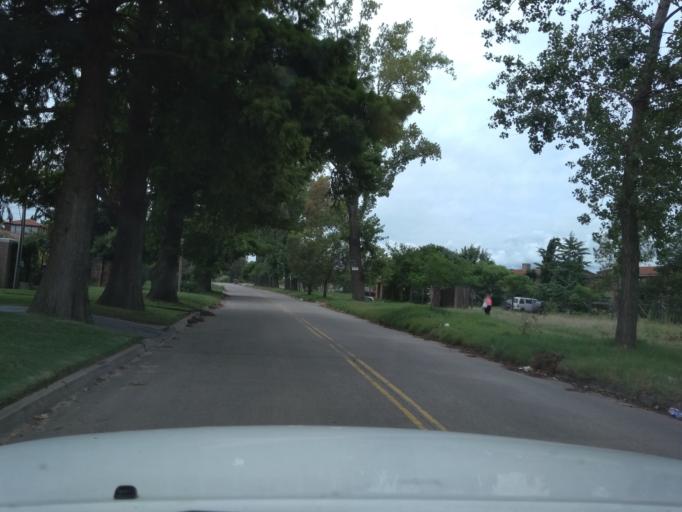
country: UY
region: Canelones
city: Paso de Carrasco
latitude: -34.8710
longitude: -56.0588
